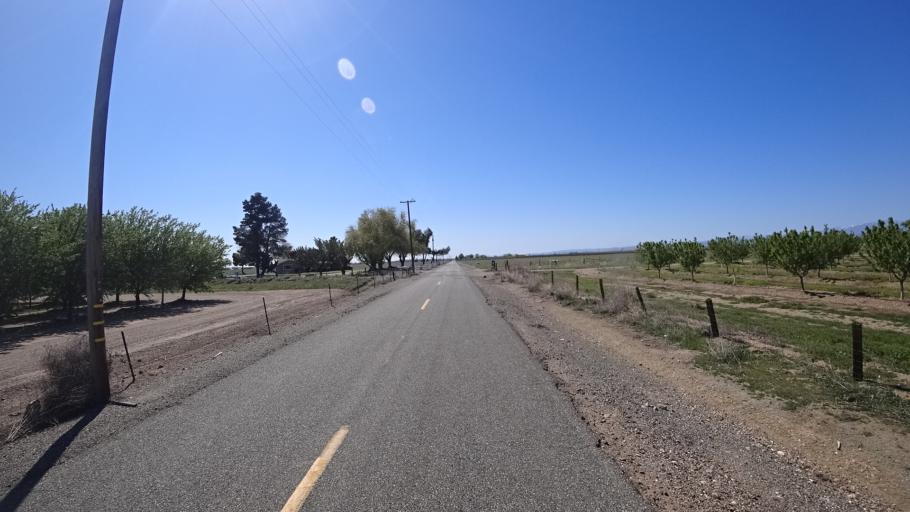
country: US
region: California
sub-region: Glenn County
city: Orland
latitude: 39.6398
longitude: -122.2534
